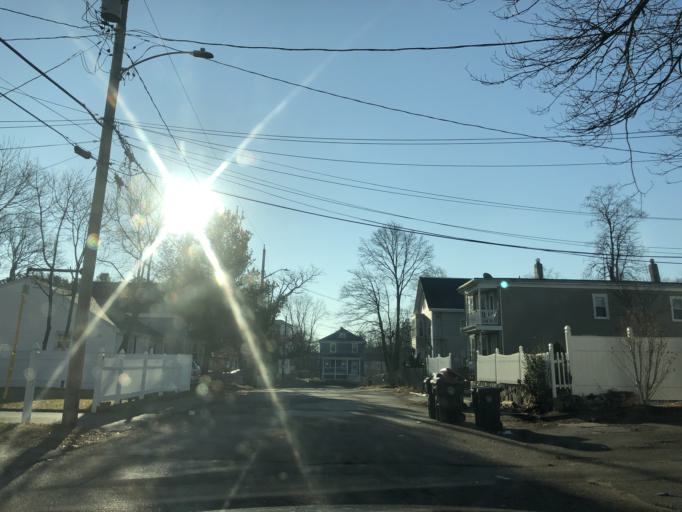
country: US
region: Massachusetts
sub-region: Plymouth County
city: Brockton
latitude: 42.1007
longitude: -71.0236
